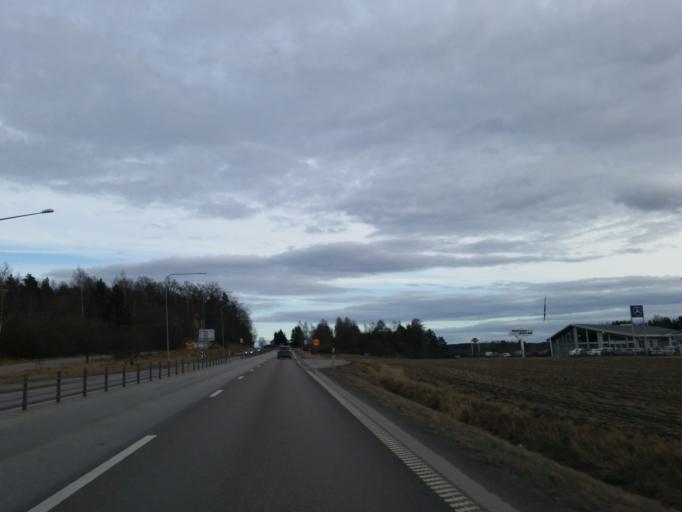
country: SE
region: OEstergoetland
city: Lindo
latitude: 58.5557
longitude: 16.2360
